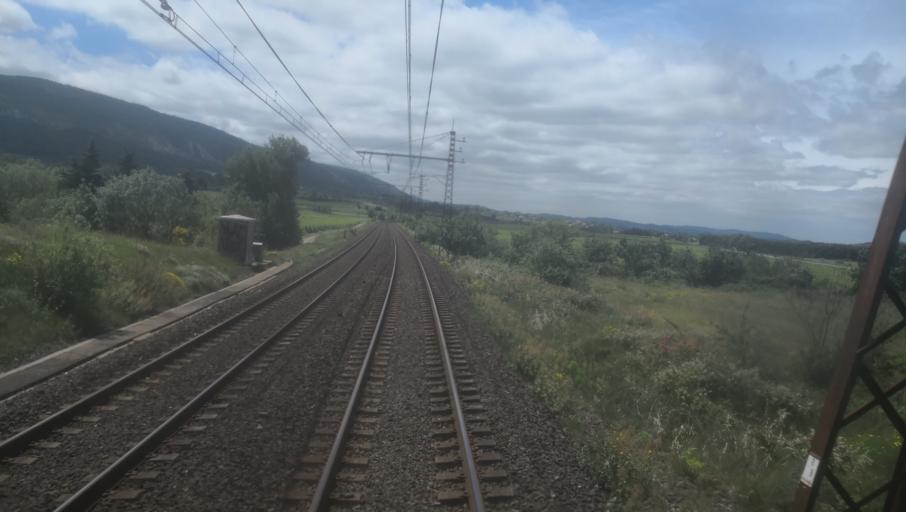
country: FR
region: Languedoc-Roussillon
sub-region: Departement de l'Aude
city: Capendu
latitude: 43.1860
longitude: 2.5367
